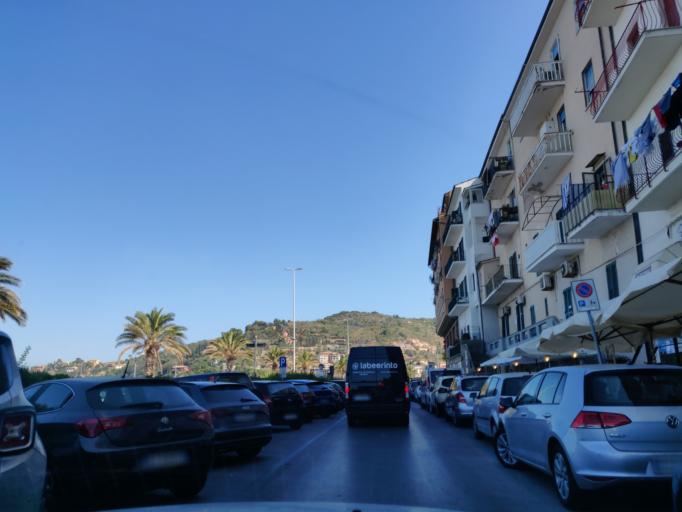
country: IT
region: Tuscany
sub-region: Provincia di Grosseto
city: Porto Santo Stefano
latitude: 42.4394
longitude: 11.1184
